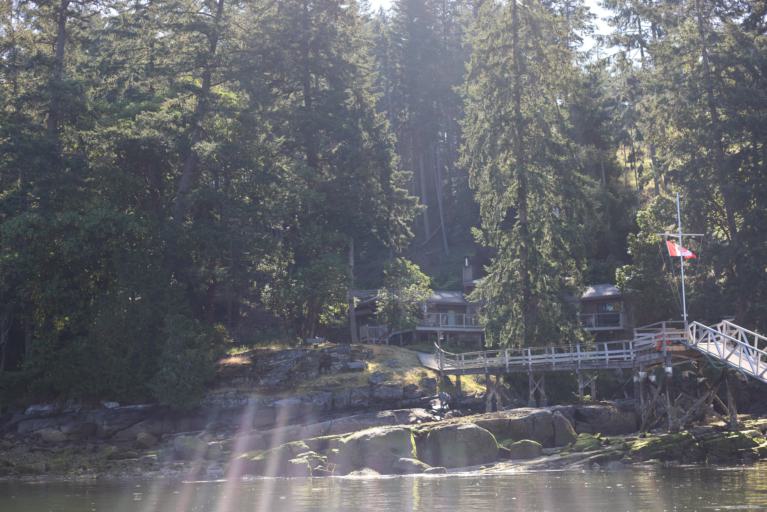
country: CA
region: British Columbia
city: North Cowichan
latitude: 48.7994
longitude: -123.5972
